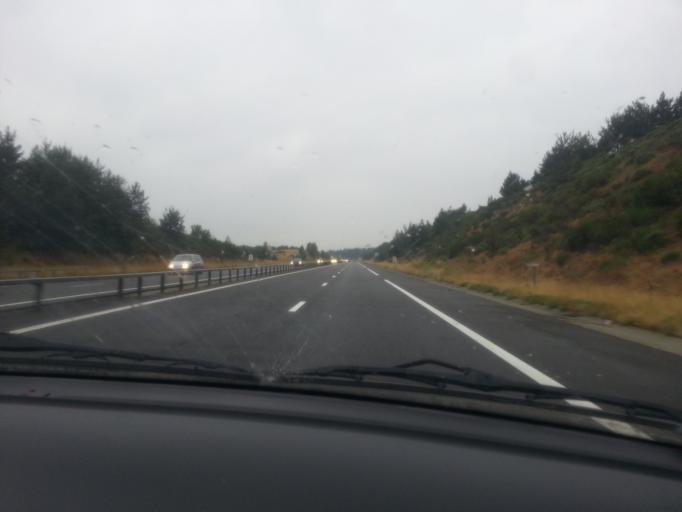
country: FR
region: Languedoc-Roussillon
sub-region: Departement de la Lozere
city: Aumont-Aubrac
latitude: 44.7561
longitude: 3.2874
